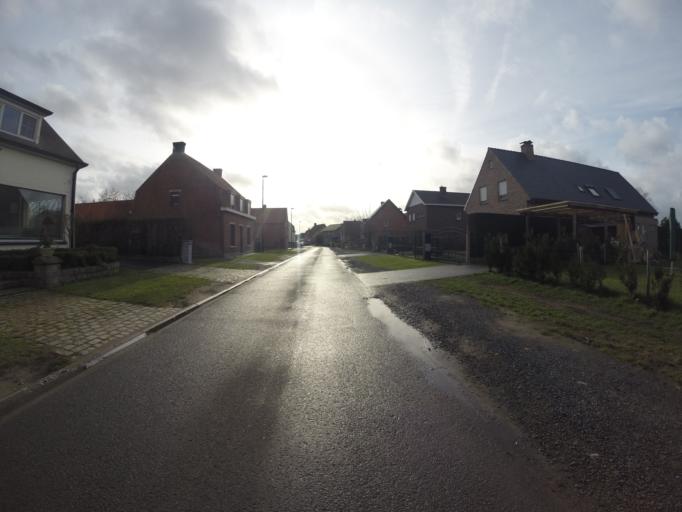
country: BE
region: Flanders
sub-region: Provincie Oost-Vlaanderen
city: Knesselare
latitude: 51.1487
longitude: 3.4135
